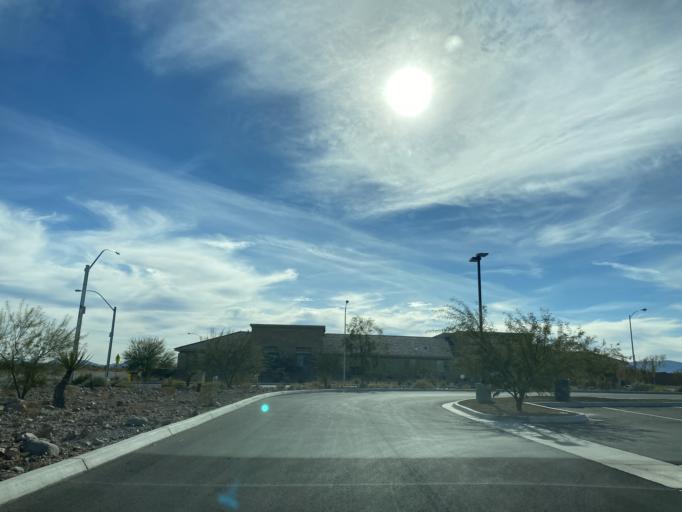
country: US
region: Nevada
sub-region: Clark County
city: Enterprise
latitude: 36.0487
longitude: -115.2706
